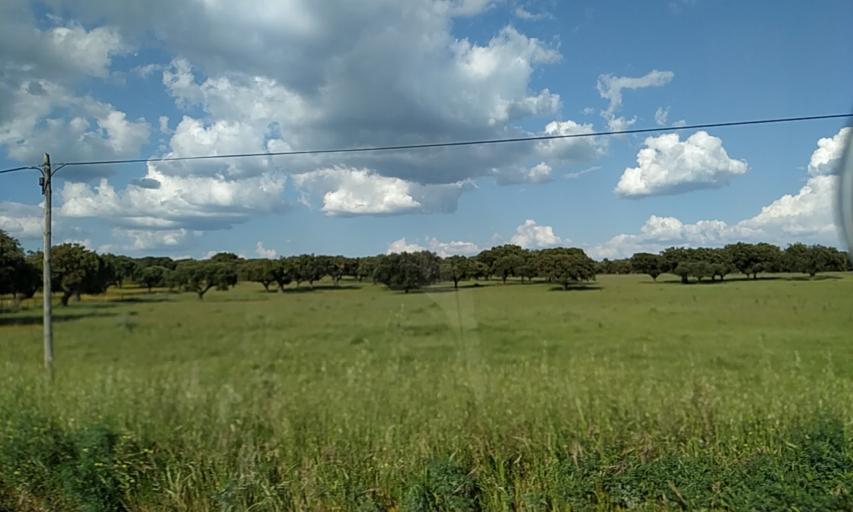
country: PT
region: Portalegre
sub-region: Portalegre
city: Urra
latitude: 39.1758
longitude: -7.4540
